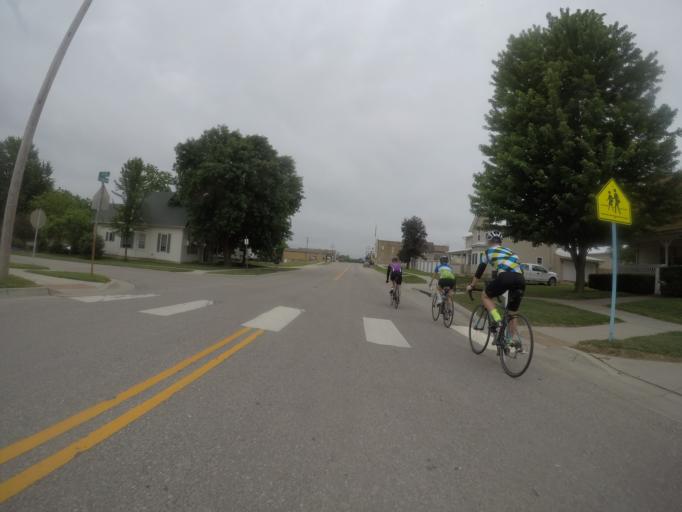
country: US
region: Kansas
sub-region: Pottawatomie County
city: Westmoreland
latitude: 39.4918
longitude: -96.1699
